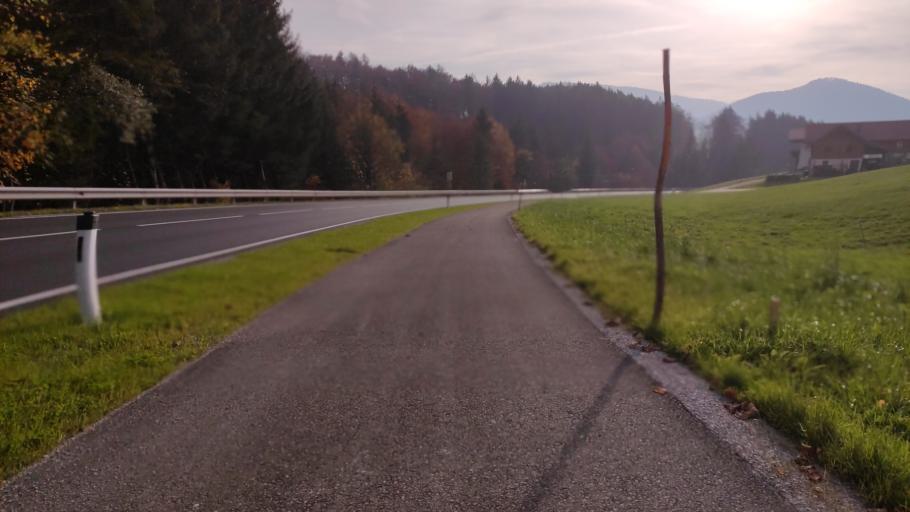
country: AT
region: Salzburg
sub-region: Politischer Bezirk Salzburg-Umgebung
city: Ebenau
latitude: 47.8017
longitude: 13.1958
